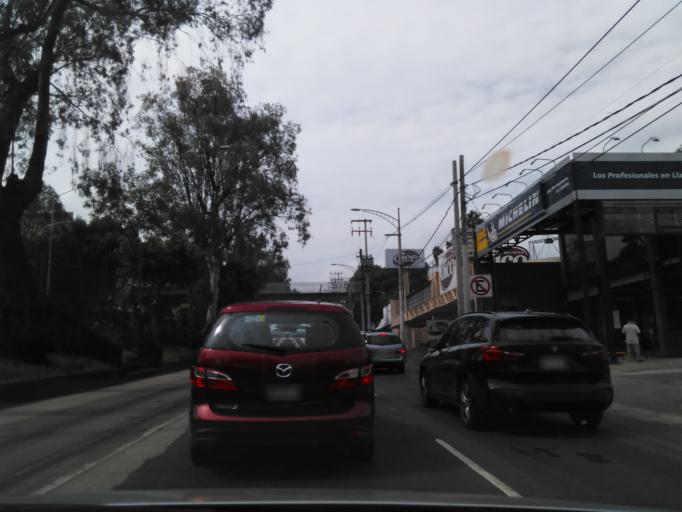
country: MX
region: Mexico City
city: Tlalpan
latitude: 19.2915
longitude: -99.1749
